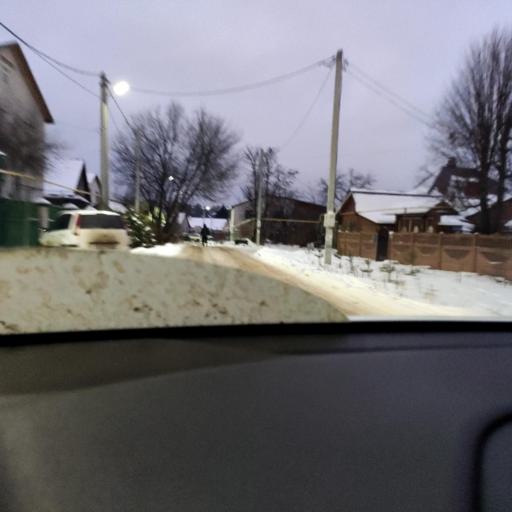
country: RU
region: Tatarstan
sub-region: Gorod Kazan'
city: Kazan
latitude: 55.8793
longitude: 49.0784
